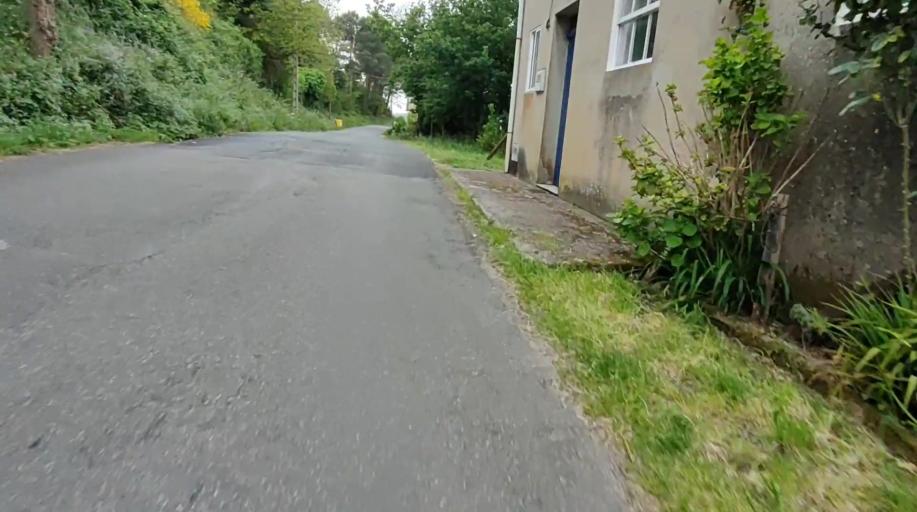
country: ES
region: Galicia
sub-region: Provincia da Coruna
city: Boiro
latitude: 42.6224
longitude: -8.8842
